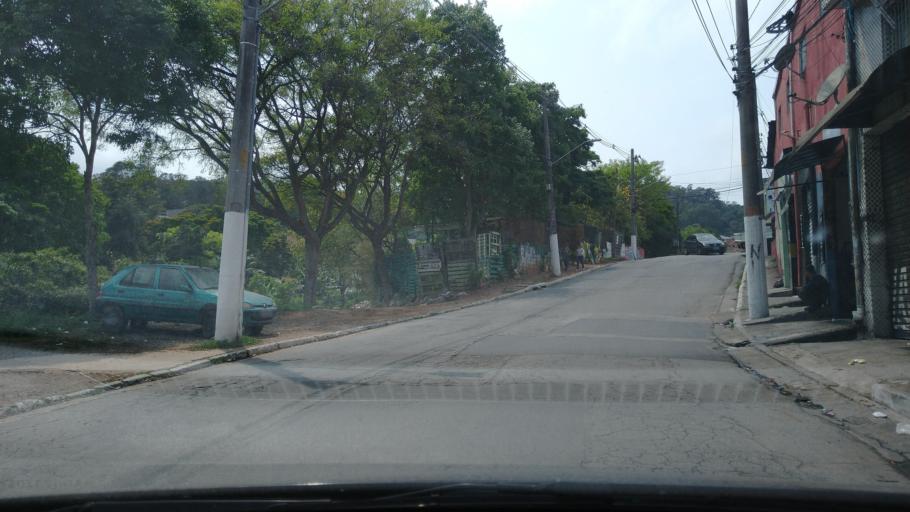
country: BR
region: Sao Paulo
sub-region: Caieiras
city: Caieiras
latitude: -23.4401
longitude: -46.7112
